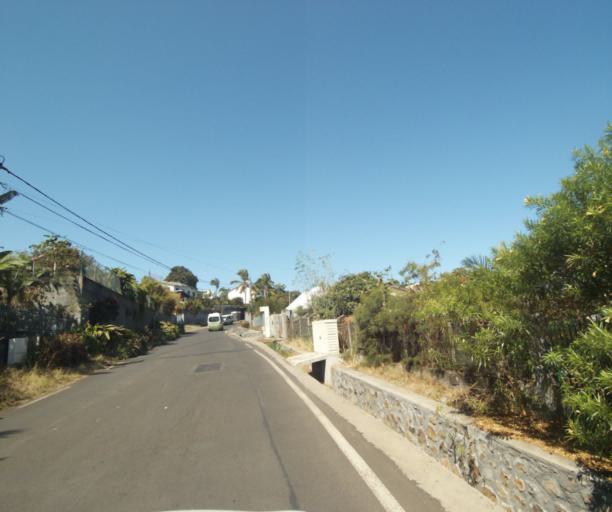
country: RE
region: Reunion
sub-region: Reunion
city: La Possession
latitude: -20.9851
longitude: 55.3255
